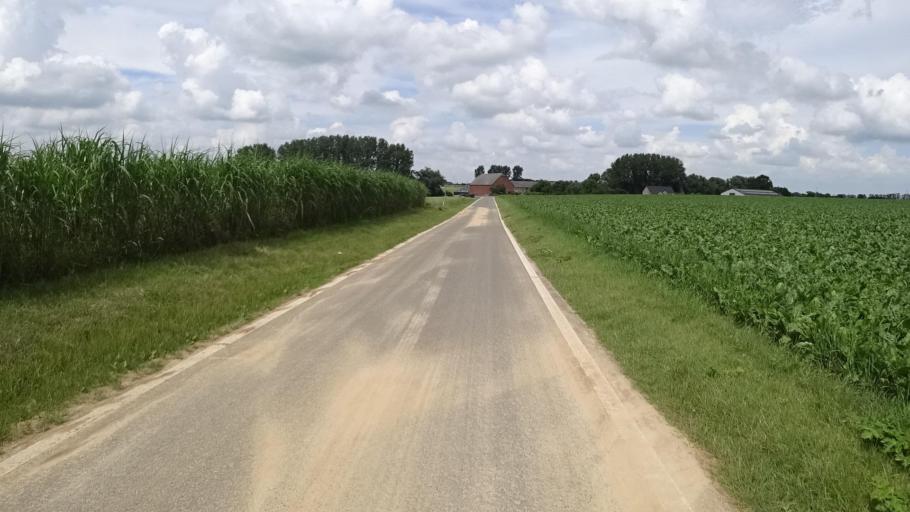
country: BE
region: Wallonia
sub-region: Province du Brabant Wallon
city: Perwez
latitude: 50.5551
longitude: 4.8329
